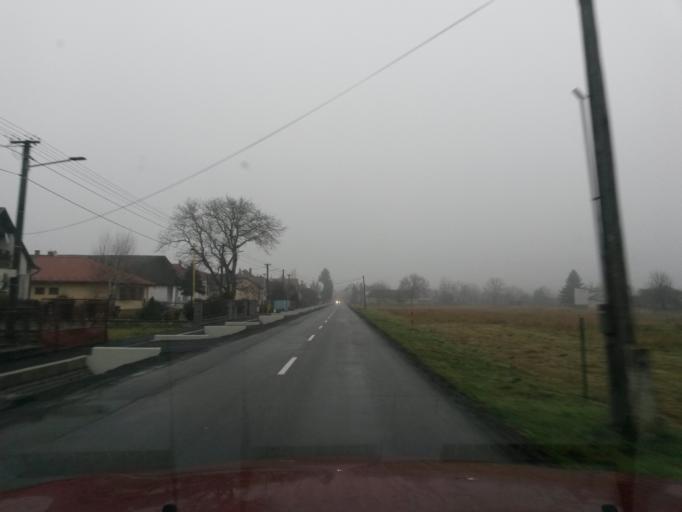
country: SK
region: Presovsky
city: Vranov nad Topl'ou
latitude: 48.8742
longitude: 21.7252
